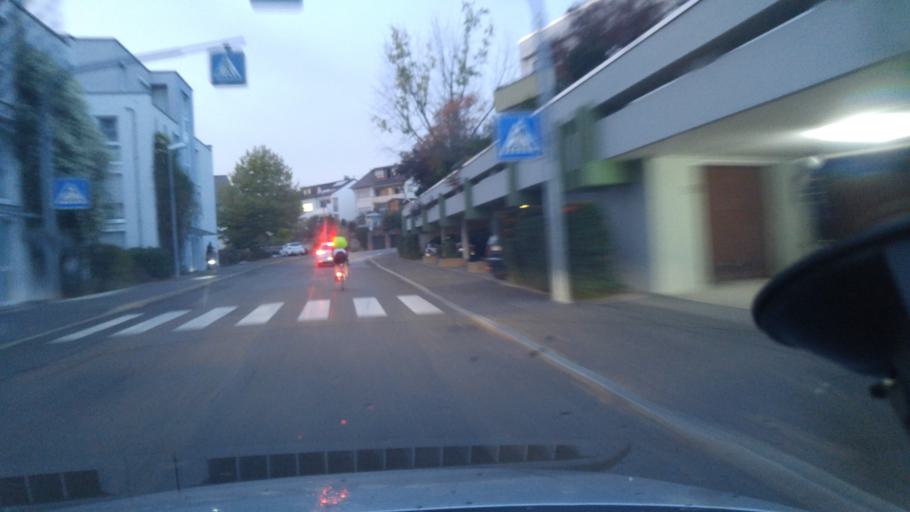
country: DE
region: Baden-Wuerttemberg
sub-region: Regierungsbezirk Stuttgart
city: Ditzingen
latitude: 48.8277
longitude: 9.0736
